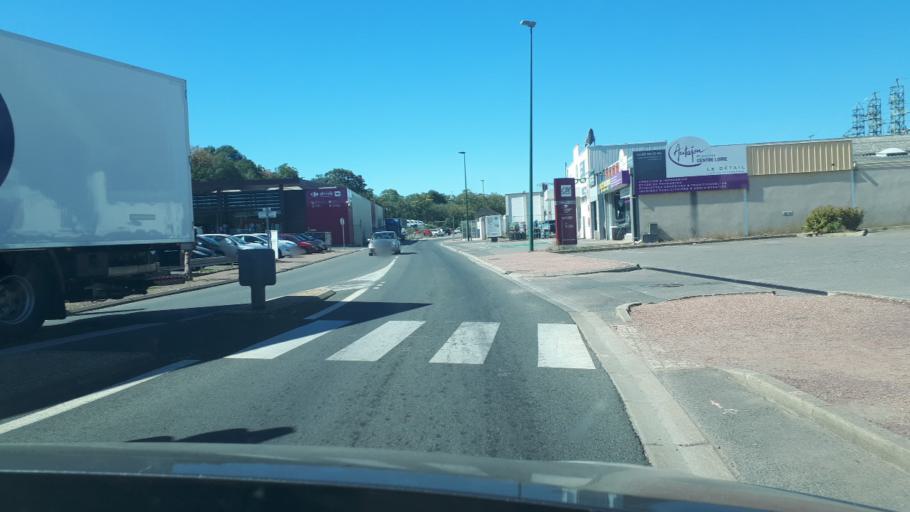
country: FR
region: Centre
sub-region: Departement du Cher
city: Saint-Satur
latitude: 47.3385
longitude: 2.8377
